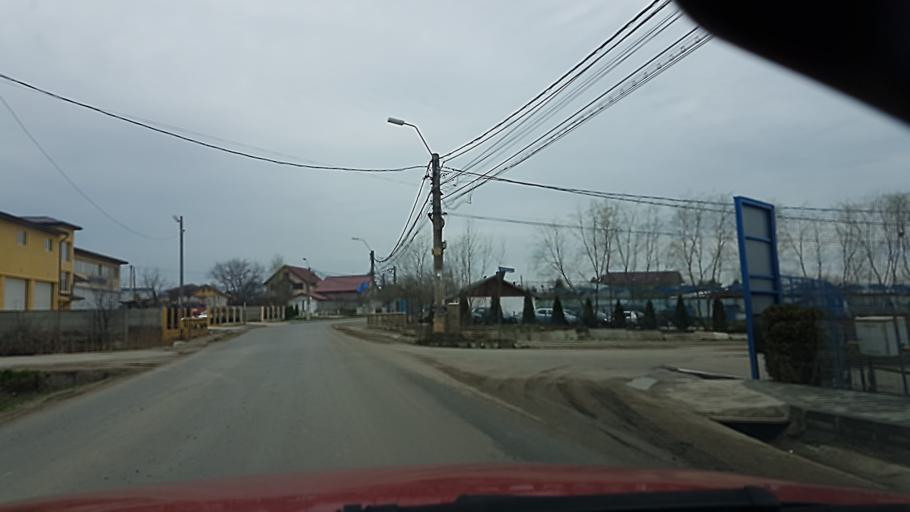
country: RO
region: Ilfov
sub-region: Comuna Tunari
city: Tunari
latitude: 44.5529
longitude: 26.1433
